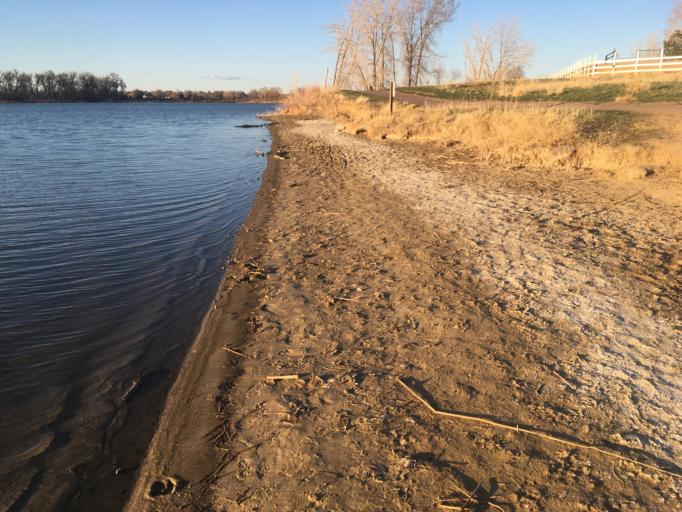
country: US
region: Colorado
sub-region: Adams County
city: Northglenn
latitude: 39.9517
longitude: -105.0108
